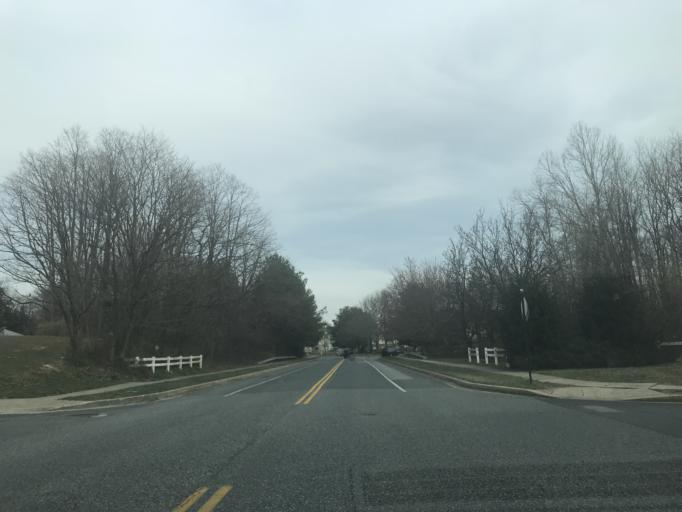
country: US
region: Maryland
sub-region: Harford County
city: South Bel Air
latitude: 39.5410
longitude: -76.3194
